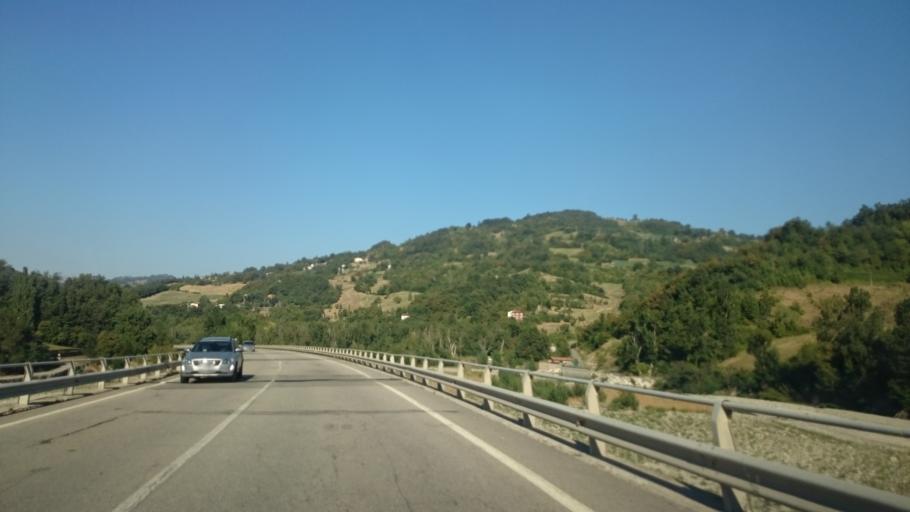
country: IT
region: Emilia-Romagna
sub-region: Provincia di Modena
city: Montefiorino
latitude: 44.4080
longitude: 10.6214
